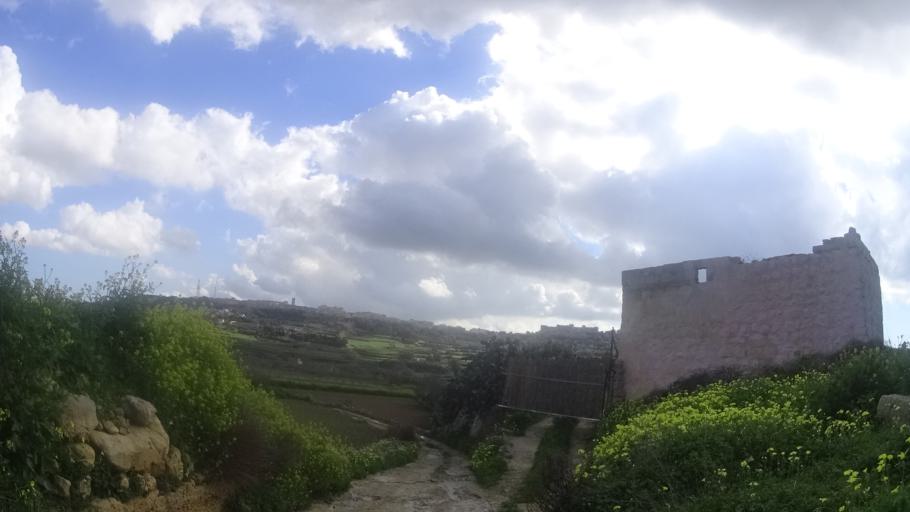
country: MT
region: L-Imtarfa
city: Imtarfa
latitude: 35.8974
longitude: 14.3892
